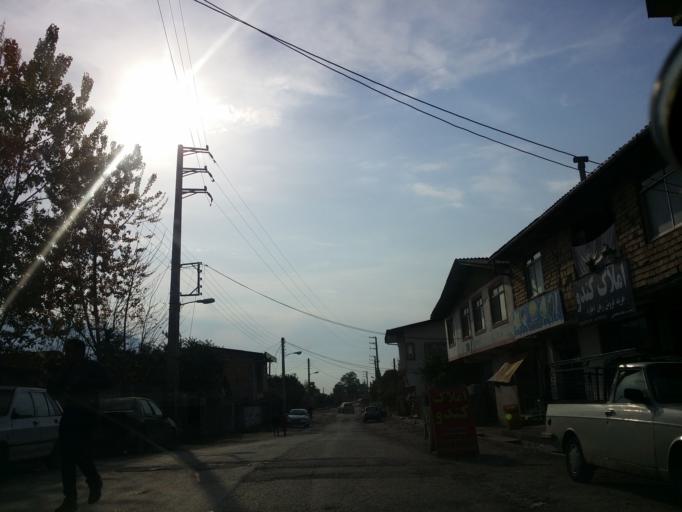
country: IR
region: Mazandaran
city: Chalus
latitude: 36.6570
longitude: 51.3950
